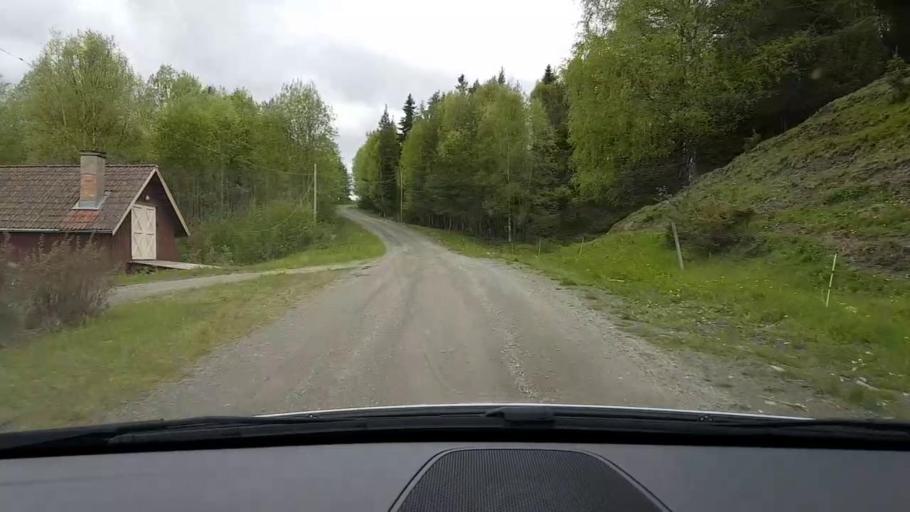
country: SE
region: Jaemtland
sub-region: Bergs Kommun
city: Hoverberg
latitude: 62.8224
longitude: 14.4032
